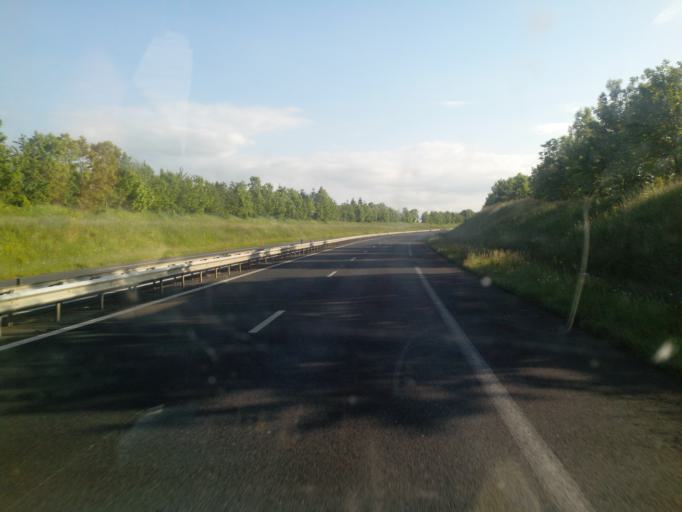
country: FR
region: Lower Normandy
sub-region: Departement du Calvados
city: Grainville-sur-Odon
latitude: 49.1226
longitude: -0.5726
